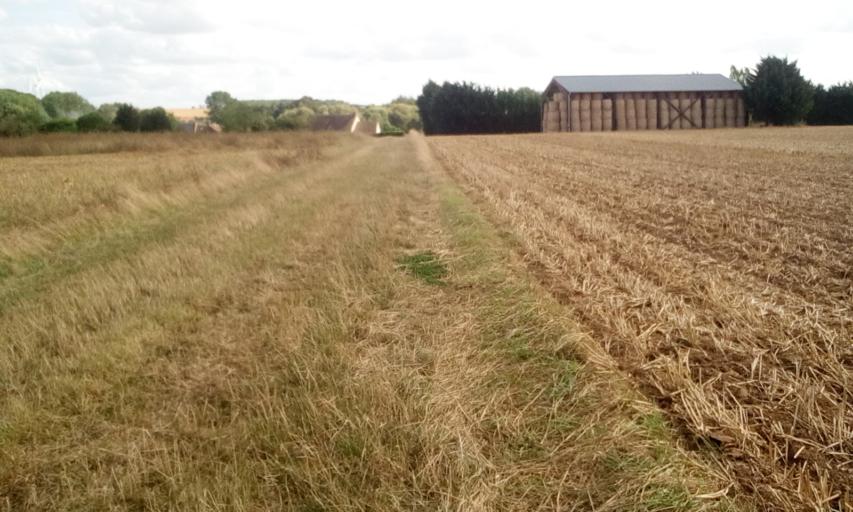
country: FR
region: Lower Normandy
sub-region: Departement du Calvados
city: Saint-Sylvain
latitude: 49.0746
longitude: -0.1960
